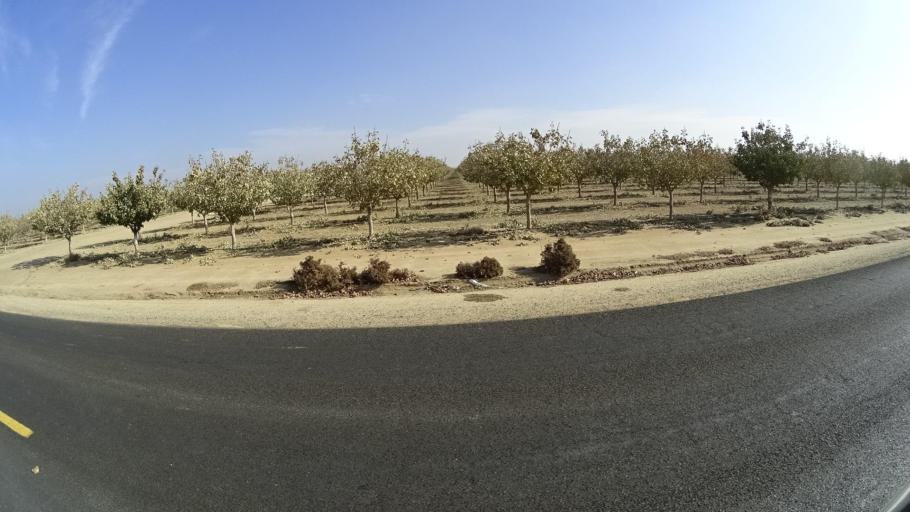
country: US
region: California
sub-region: Kern County
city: Shafter
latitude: 35.5404
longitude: -119.1513
